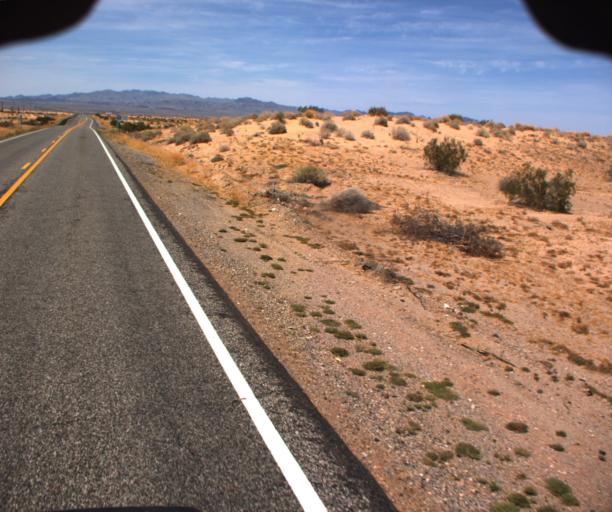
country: US
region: Arizona
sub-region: La Paz County
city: Parker
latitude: 34.0817
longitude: -114.2683
